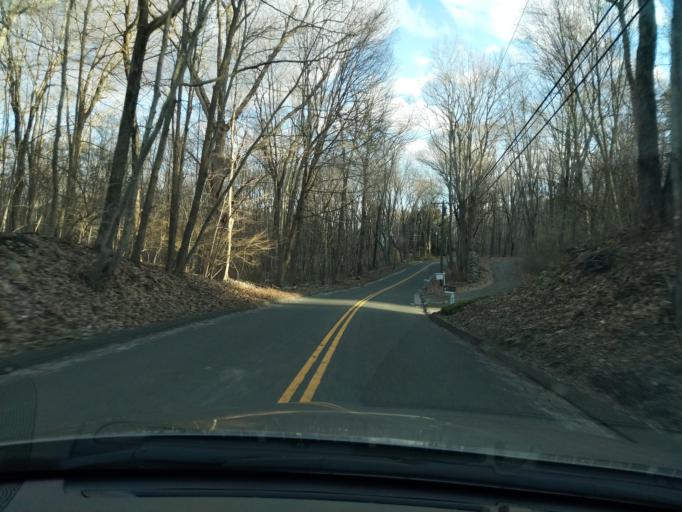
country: US
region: Connecticut
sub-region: Fairfield County
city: Newtown
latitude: 41.3749
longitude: -73.2827
